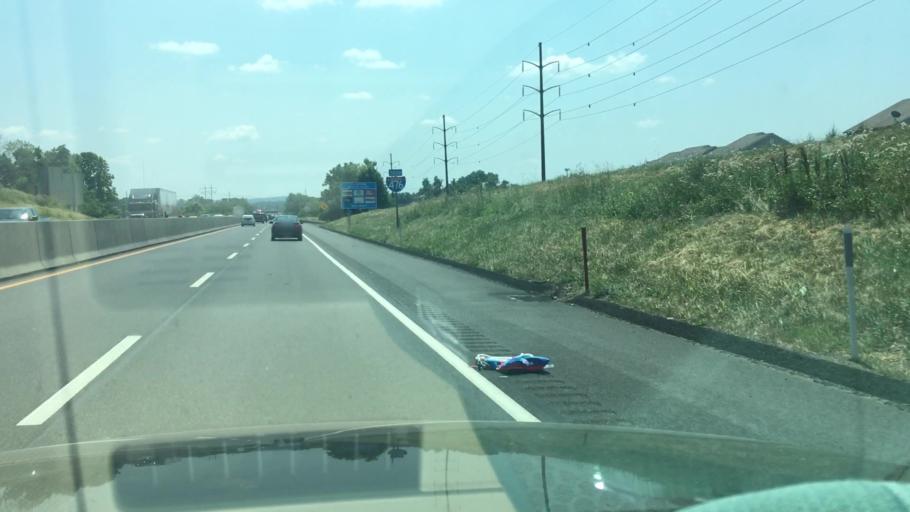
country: US
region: Pennsylvania
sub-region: Lehigh County
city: Wescosville
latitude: 40.5865
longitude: -75.5631
